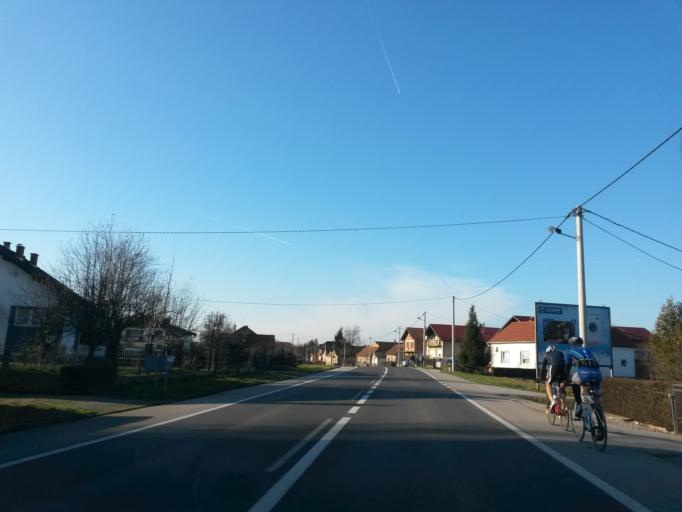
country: HR
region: Varazdinska
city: Ludbreg
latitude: 46.2622
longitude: 16.5803
